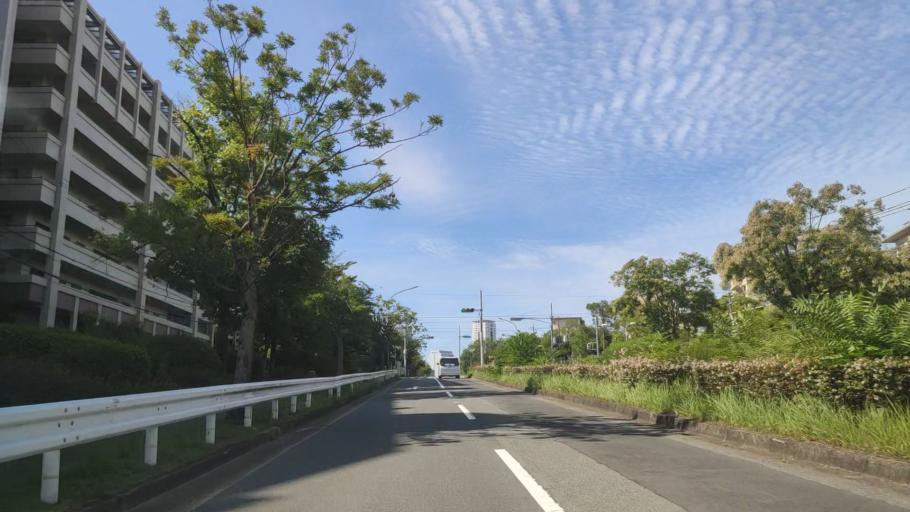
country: JP
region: Osaka
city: Mino
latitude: 34.8191
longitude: 135.5065
